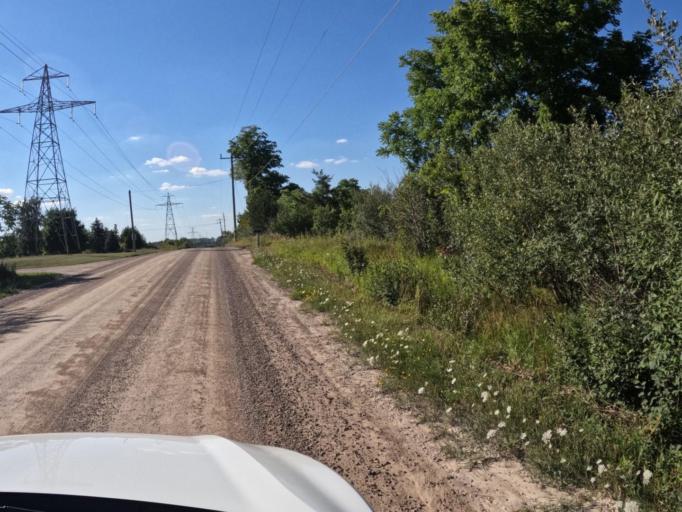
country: CA
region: Ontario
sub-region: Wellington County
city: Guelph
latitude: 43.4426
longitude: -80.1465
